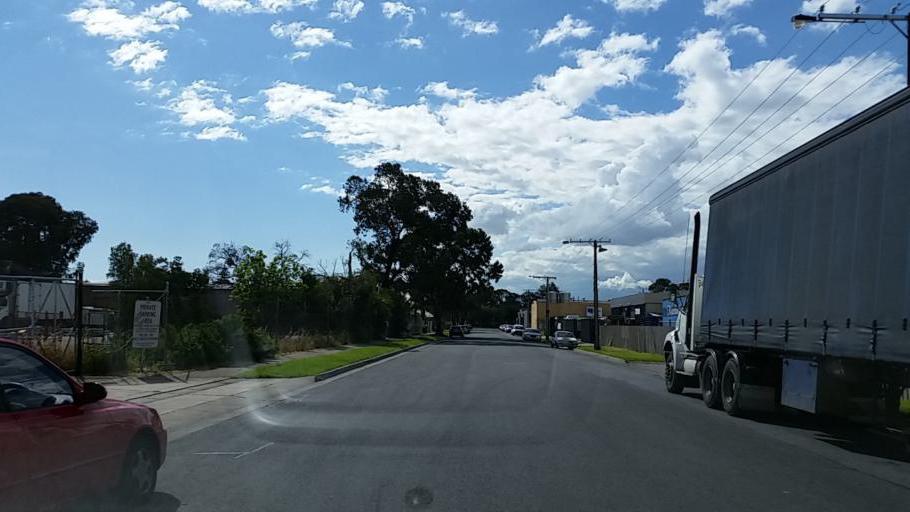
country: AU
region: South Australia
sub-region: Charles Sturt
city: Albert Park
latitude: -34.8759
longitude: 138.5237
